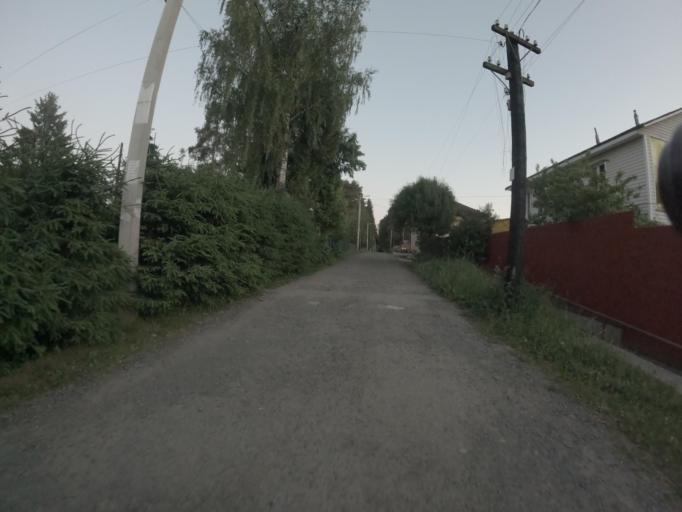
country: RU
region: Leningrad
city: Vsevolozhsk
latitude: 60.0186
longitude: 30.6176
